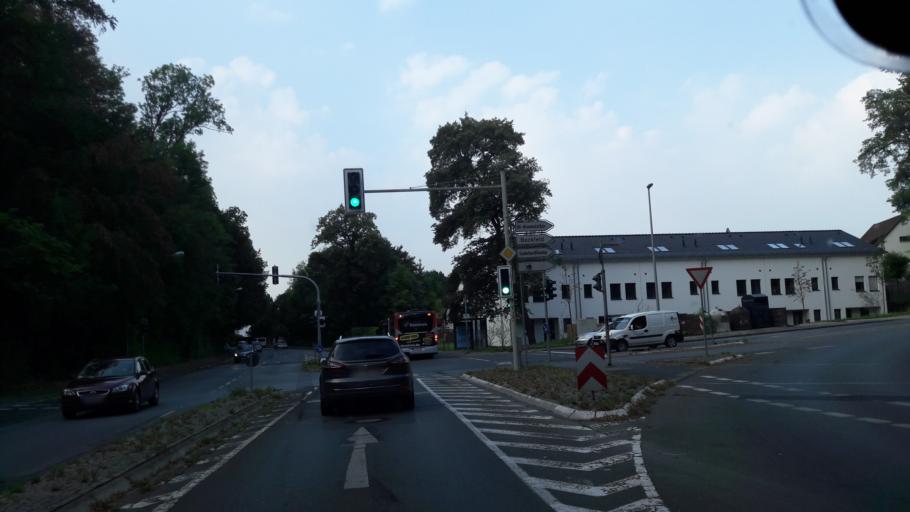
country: DE
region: Lower Saxony
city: Hildesheim
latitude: 52.1407
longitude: 9.9303
